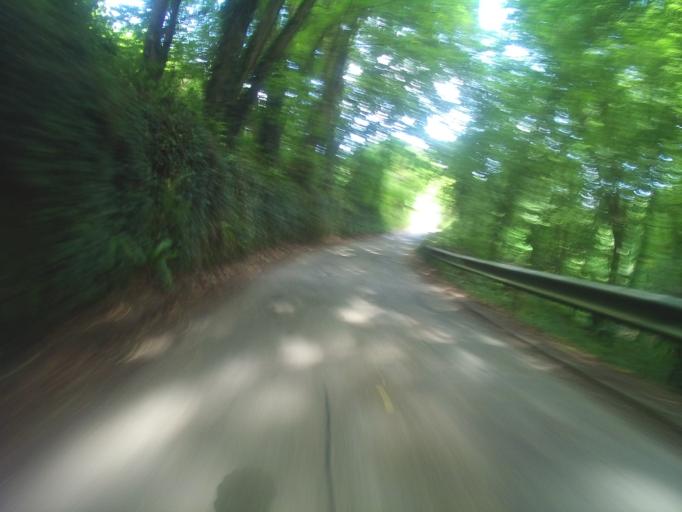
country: GB
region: England
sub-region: Devon
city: Buckfastleigh
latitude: 50.4763
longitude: -3.7607
